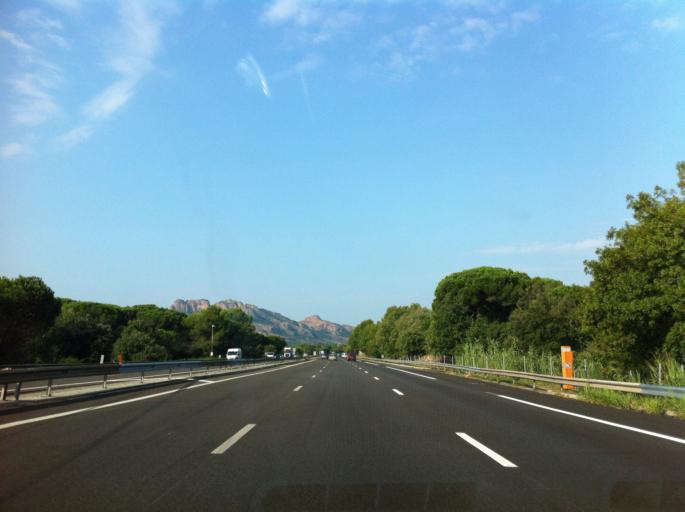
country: FR
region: Provence-Alpes-Cote d'Azur
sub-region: Departement du Var
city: Puget-sur-Argens
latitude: 43.4667
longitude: 6.6541
